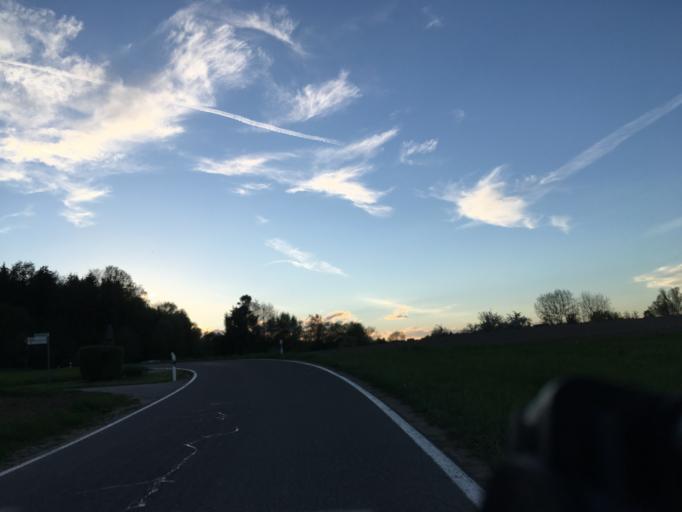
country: DE
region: Baden-Wuerttemberg
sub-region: Freiburg Region
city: Gailingen
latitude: 47.7182
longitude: 8.7611
